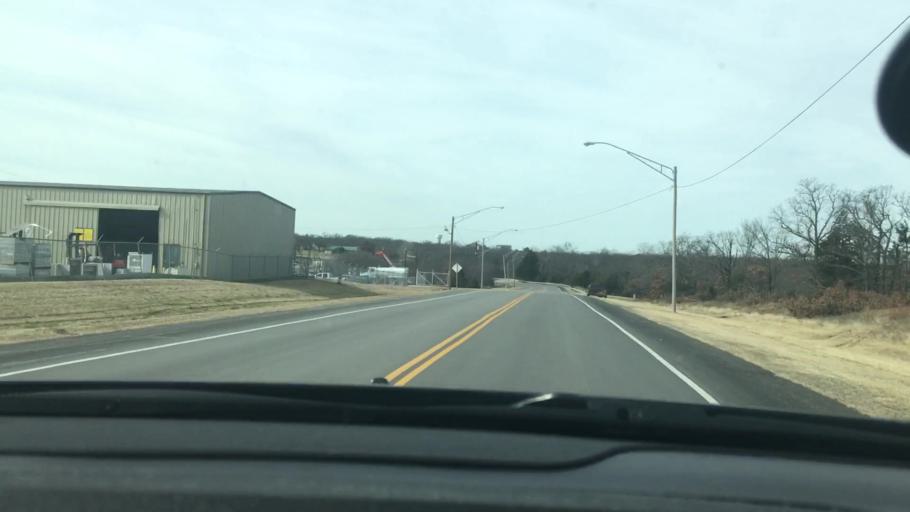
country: US
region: Oklahoma
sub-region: Carter County
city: Ardmore
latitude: 34.1749
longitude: -97.1717
